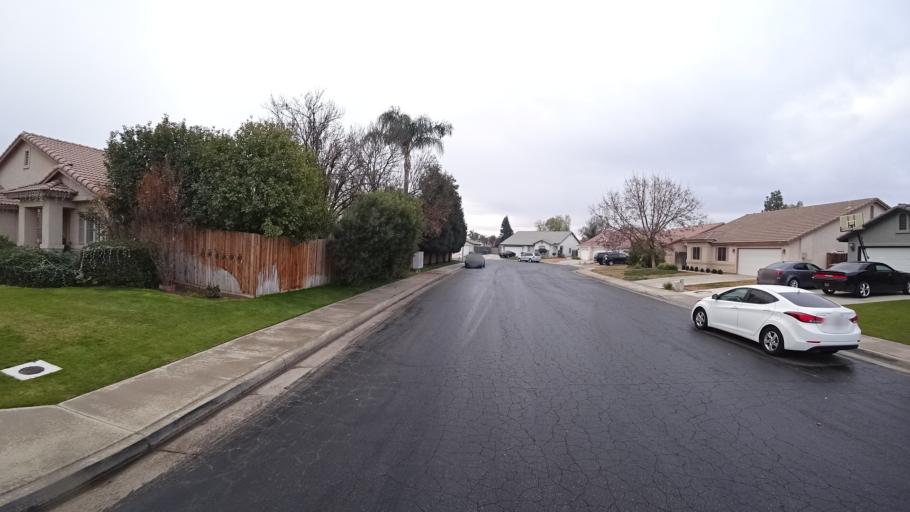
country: US
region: California
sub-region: Kern County
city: Greenfield
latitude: 35.3048
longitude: -119.0786
